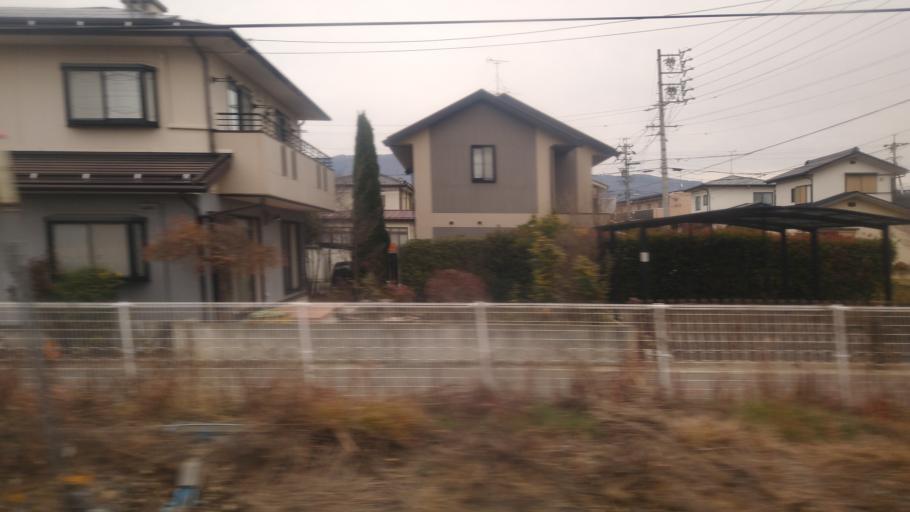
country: JP
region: Nagano
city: Shiojiri
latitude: 36.1263
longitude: 137.9484
